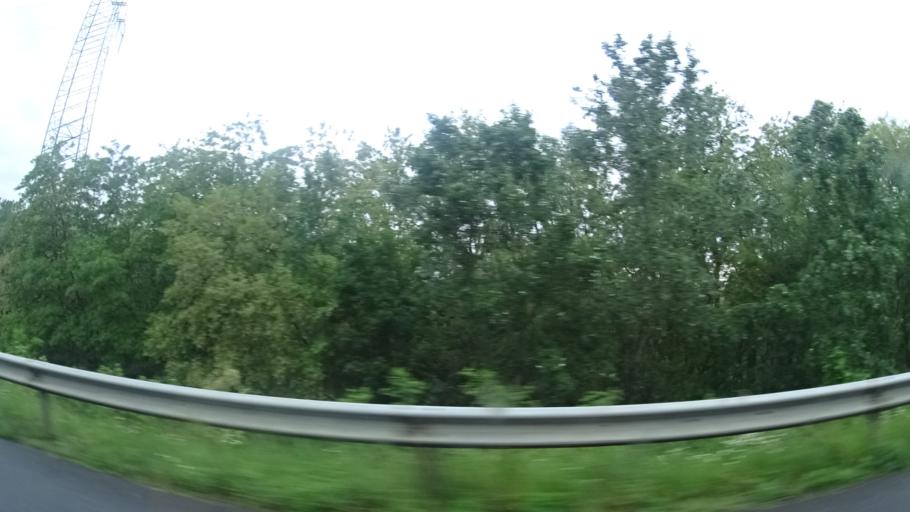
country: DE
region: Rheinland-Pfalz
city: Hordt
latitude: 49.1921
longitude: 8.3178
